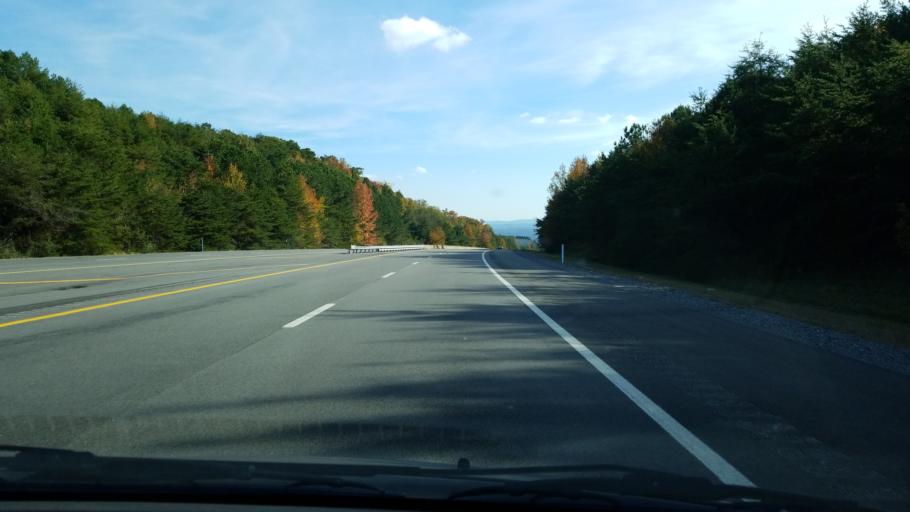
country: US
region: Tennessee
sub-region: Hamilton County
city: Sale Creek
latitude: 35.3394
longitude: -85.1677
